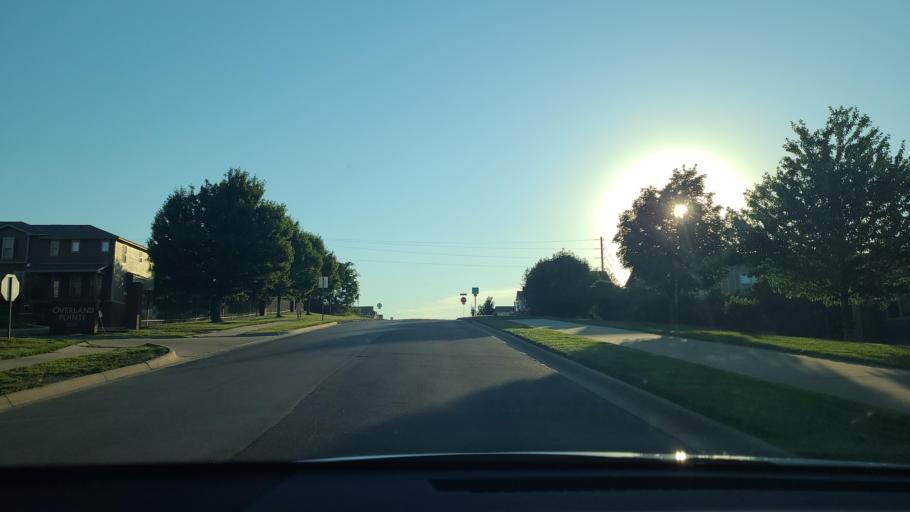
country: US
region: Kansas
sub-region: Douglas County
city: Lawrence
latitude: 38.9752
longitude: -95.3152
